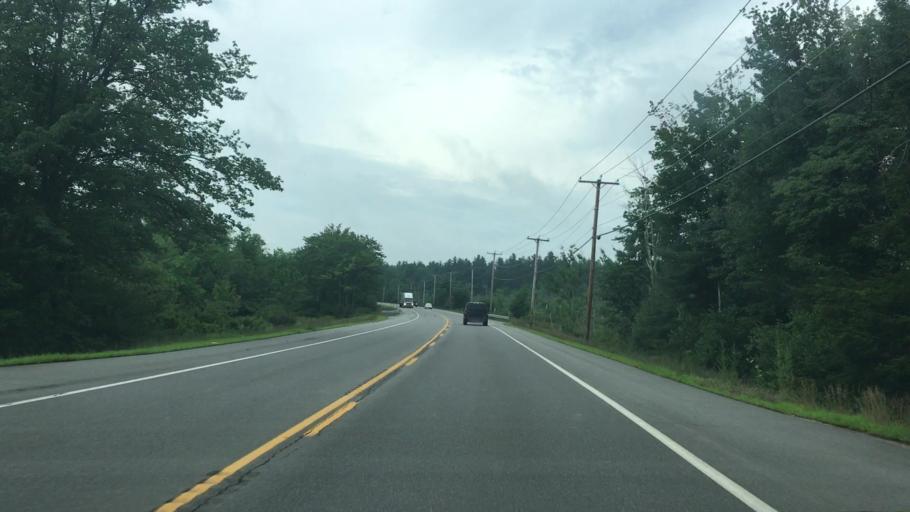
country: US
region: Maine
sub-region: York County
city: Lebanon
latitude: 43.4005
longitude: -70.8756
